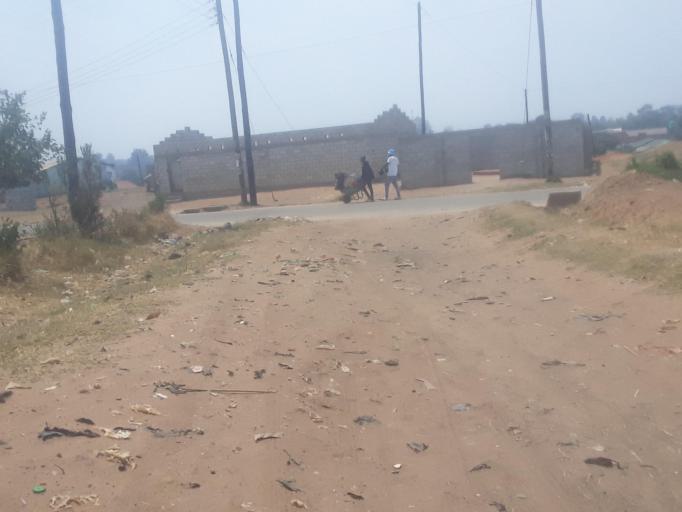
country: ZM
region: Lusaka
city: Lusaka
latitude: -15.3680
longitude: 28.2969
